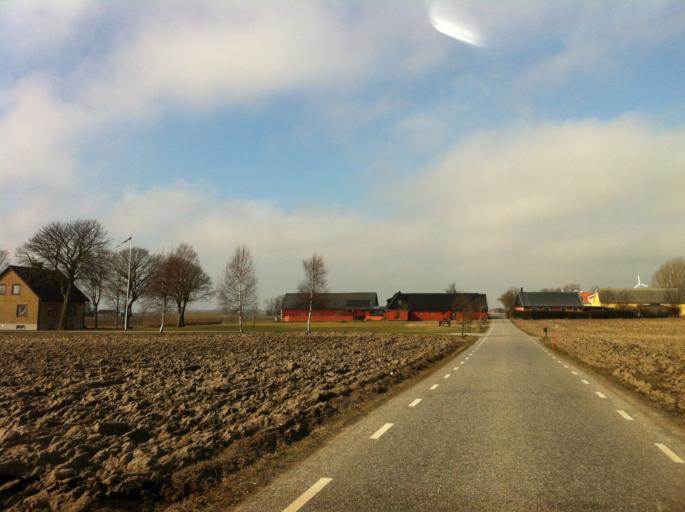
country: SE
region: Skane
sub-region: Svalovs Kommun
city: Teckomatorp
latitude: 55.8644
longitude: 13.0532
